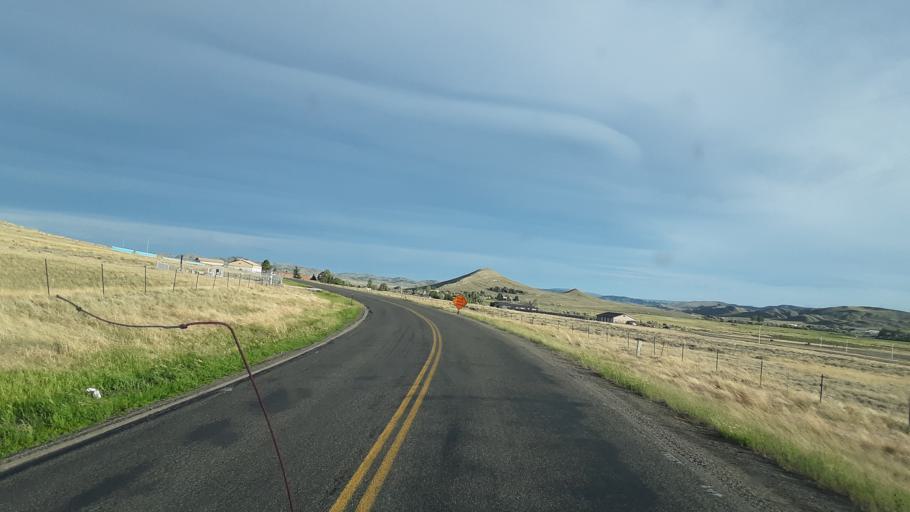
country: US
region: Wyoming
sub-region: Park County
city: Cody
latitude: 44.5175
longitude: -109.0173
